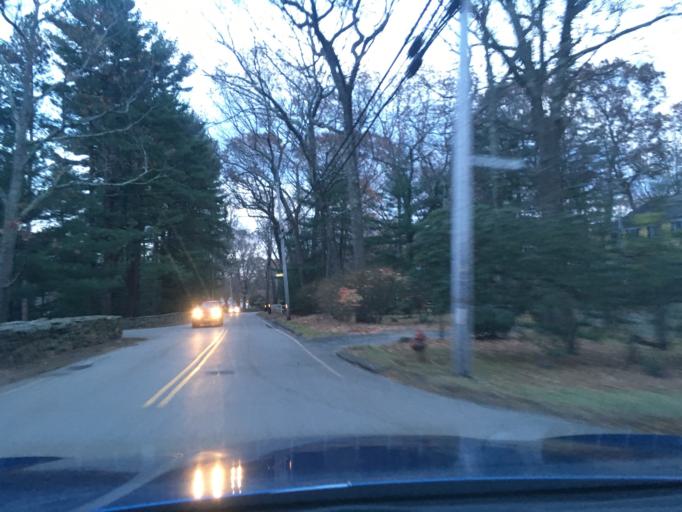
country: US
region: Rhode Island
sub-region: Kent County
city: East Greenwich
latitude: 41.6726
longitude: -71.4579
